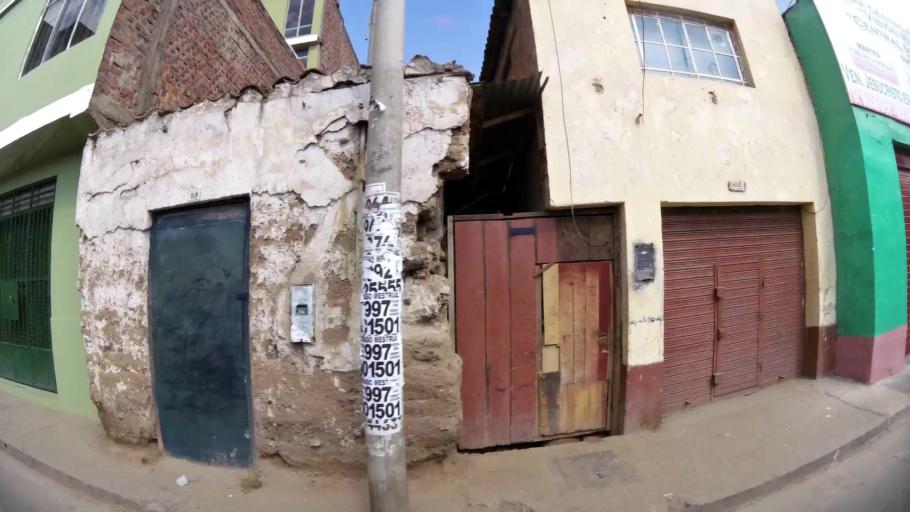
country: PE
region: Junin
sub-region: Provincia de Huancayo
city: Huancayo
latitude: -12.0745
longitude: -75.2094
